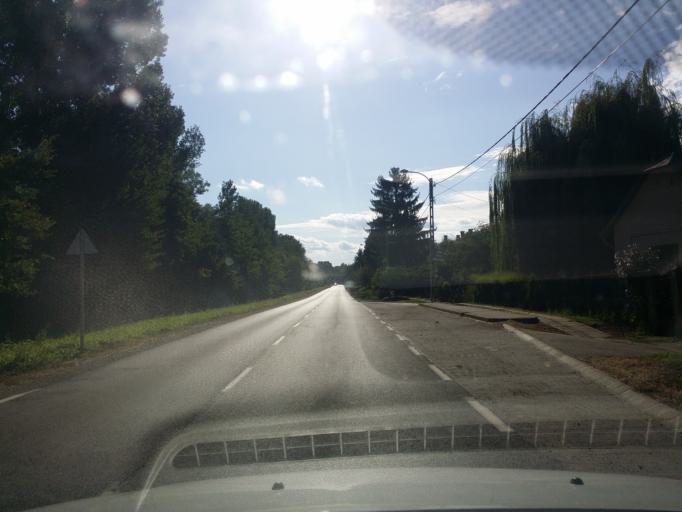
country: HU
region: Fejer
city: Mezoszilas
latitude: 46.8366
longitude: 18.5317
